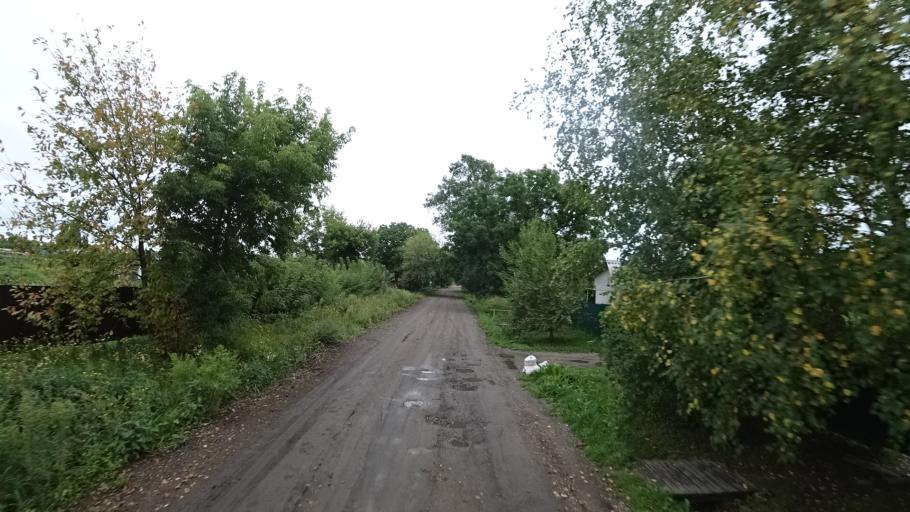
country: RU
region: Primorskiy
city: Chernigovka
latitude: 44.3394
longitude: 132.5401
